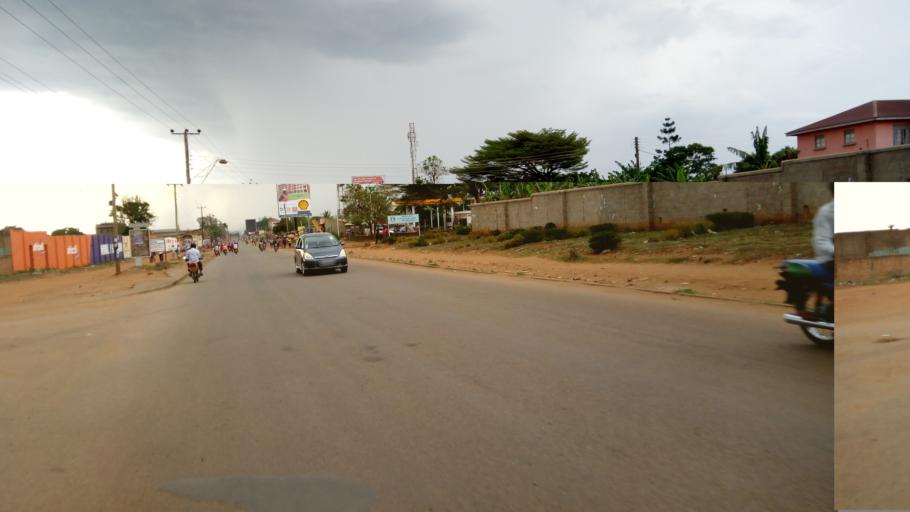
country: UG
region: Eastern Region
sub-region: Mbale District
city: Mbale
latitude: 1.0793
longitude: 34.1671
